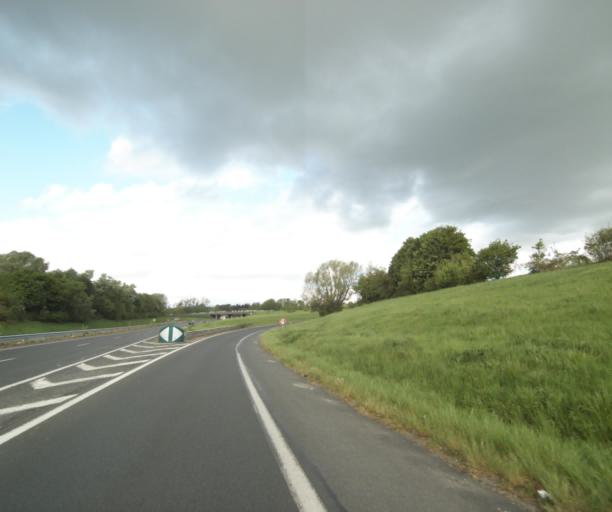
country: FR
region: Ile-de-France
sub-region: Departement de Seine-et-Marne
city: Lognes
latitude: 48.8458
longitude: 2.6368
